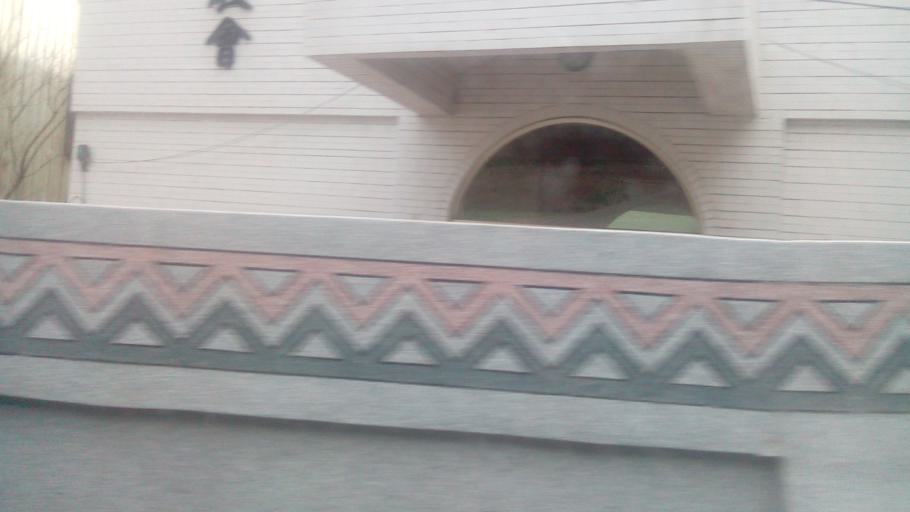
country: TW
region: Taiwan
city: Daxi
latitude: 24.4386
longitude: 121.3791
